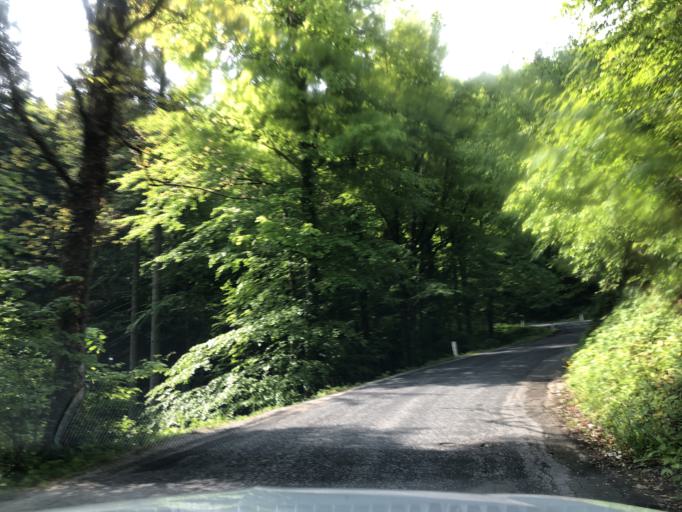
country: SI
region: Bloke
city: Nova Vas
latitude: 45.8036
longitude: 14.5648
